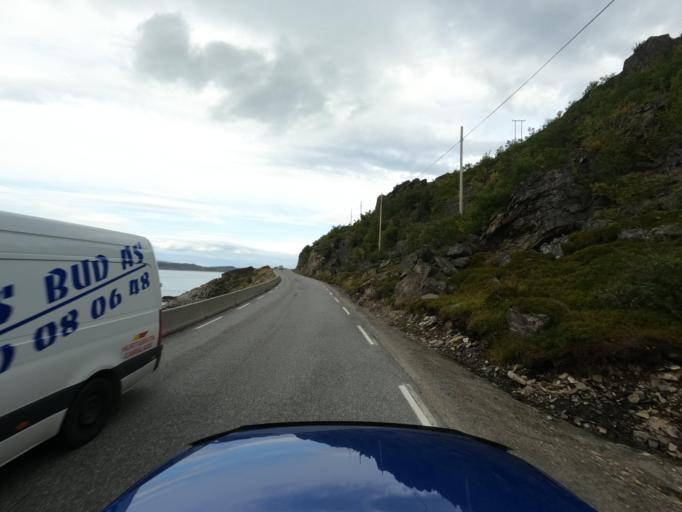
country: NO
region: Finnmark Fylke
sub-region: Hammerfest
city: Rypefjord
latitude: 70.5793
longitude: 23.6897
